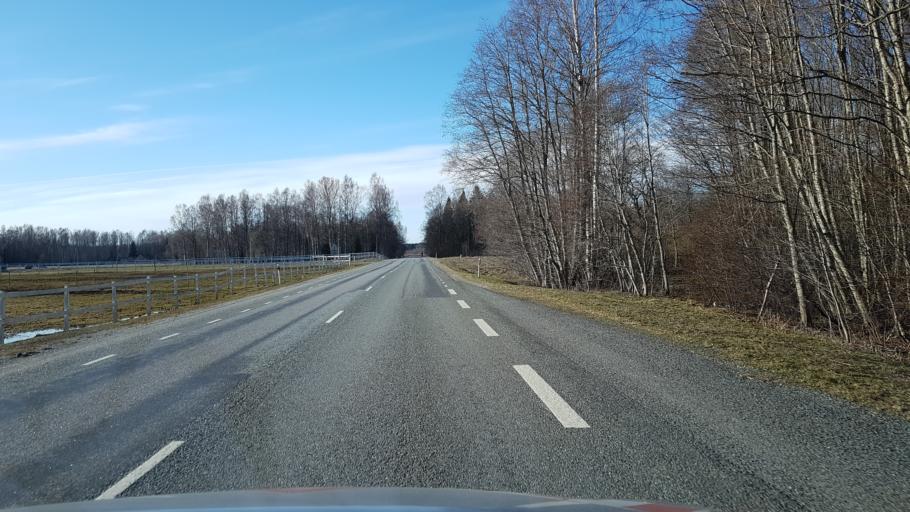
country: EE
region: Laeaene-Virumaa
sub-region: Tapa vald
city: Tapa
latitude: 59.4402
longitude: 25.9574
